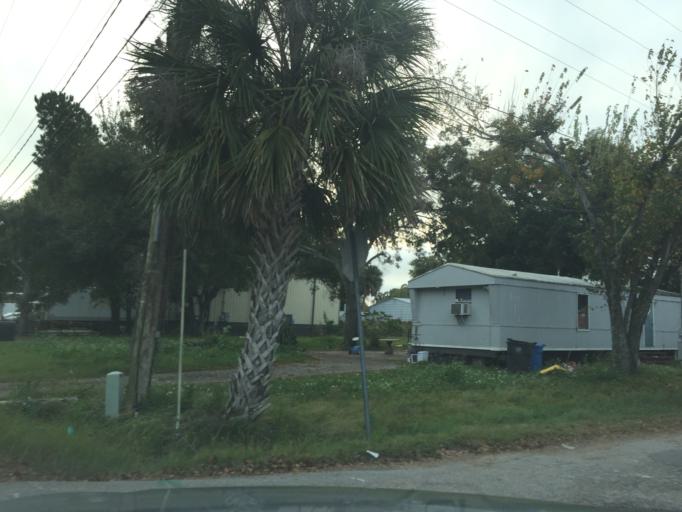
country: US
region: Florida
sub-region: Hillsborough County
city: Town 'n' Country
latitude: 27.9855
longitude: -82.5485
